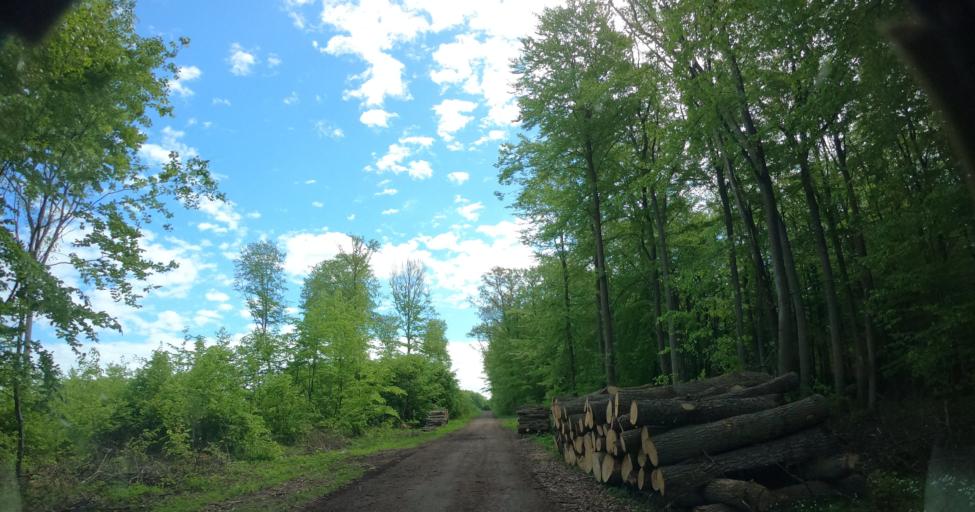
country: PL
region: West Pomeranian Voivodeship
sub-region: Powiat stargardzki
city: Dobrzany
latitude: 53.3474
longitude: 15.4907
